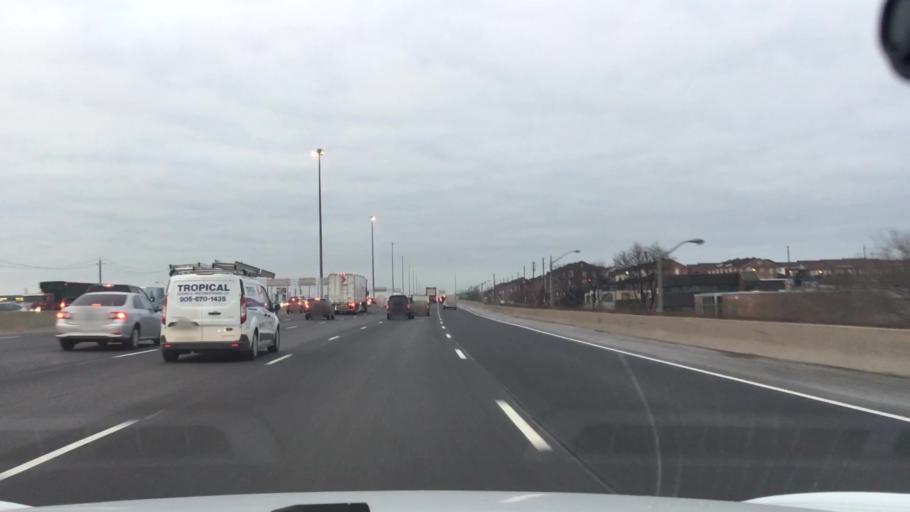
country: CA
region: Ontario
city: Etobicoke
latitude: 43.7230
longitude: -79.5229
